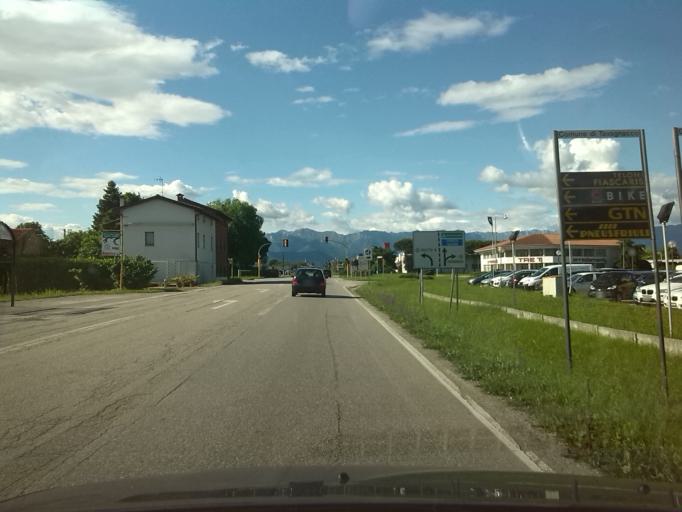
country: IT
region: Friuli Venezia Giulia
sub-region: Provincia di Udine
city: Tavagnacco
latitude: 46.1066
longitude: 13.2289
